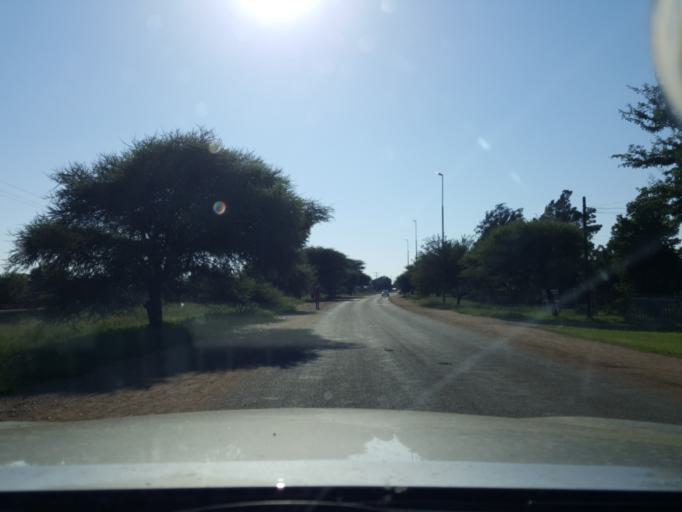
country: ZA
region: North-West
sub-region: Ngaka Modiri Molema District Municipality
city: Mmabatho
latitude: -25.8257
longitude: 25.6409
